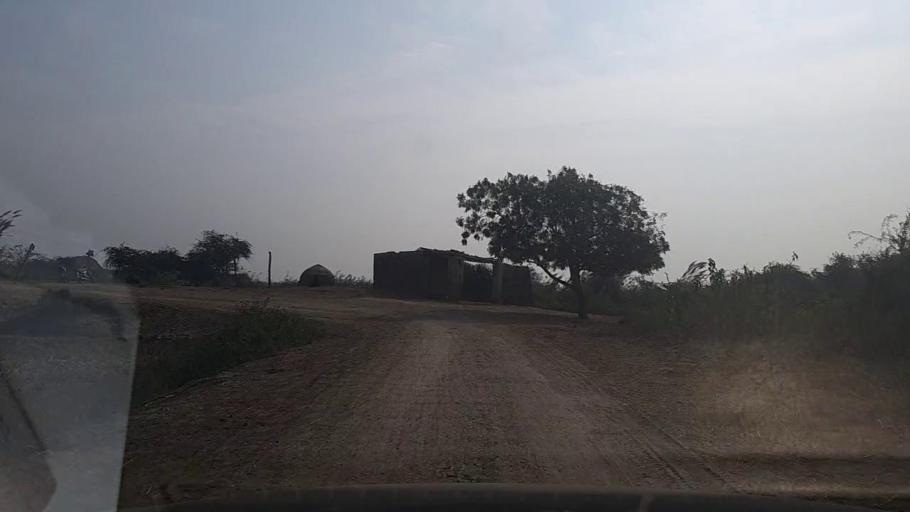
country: PK
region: Sindh
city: Bulri
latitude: 24.9423
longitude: 68.2814
